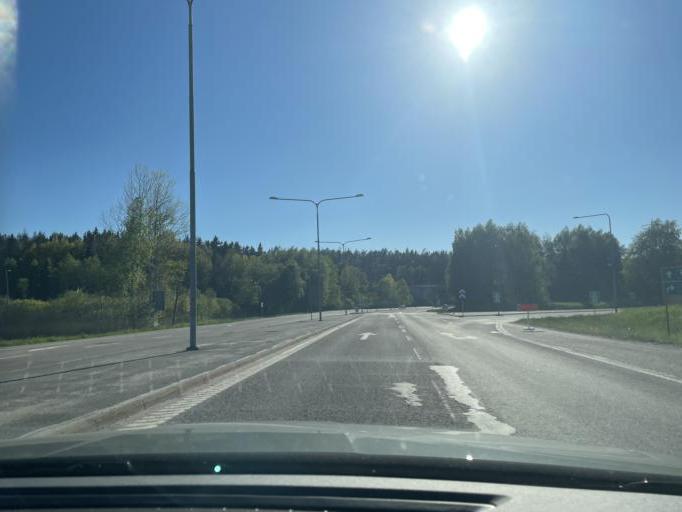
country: SE
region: Stockholm
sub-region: Haninge Kommun
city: Handen
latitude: 59.2182
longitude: 18.1399
